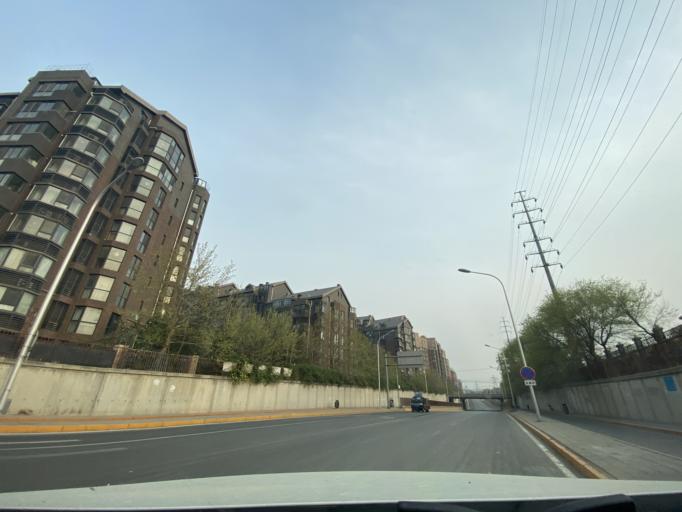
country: CN
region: Beijing
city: Babaoshan
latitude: 39.9324
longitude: 116.2325
